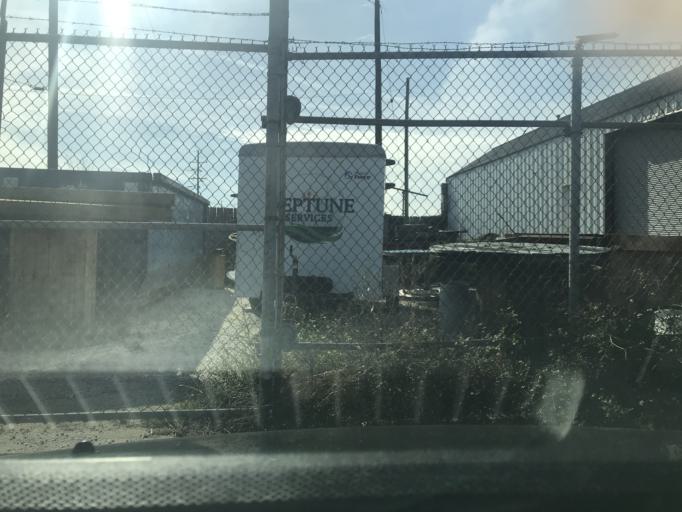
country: US
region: Louisiana
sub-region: Orleans Parish
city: New Orleans
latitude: 29.9550
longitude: -90.0941
